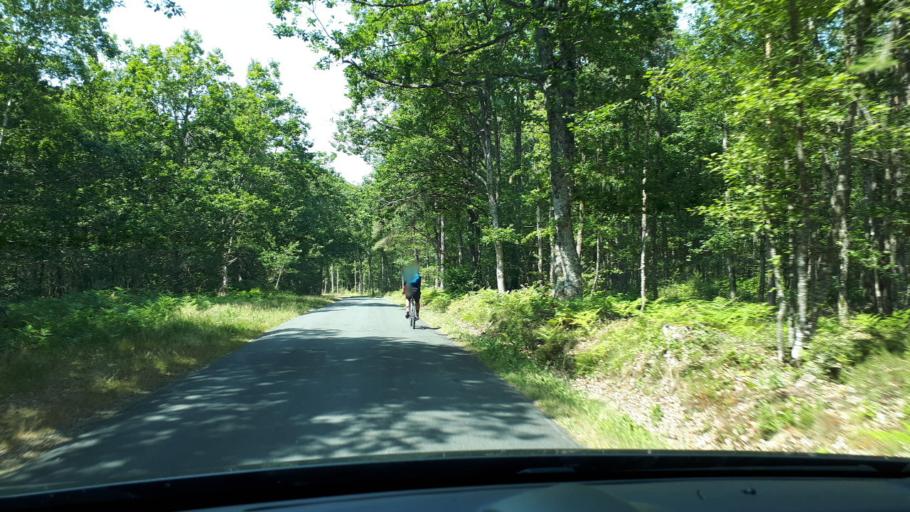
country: FR
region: Centre
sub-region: Departement du Loir-et-Cher
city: Naveil
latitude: 47.8283
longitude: 1.0401
